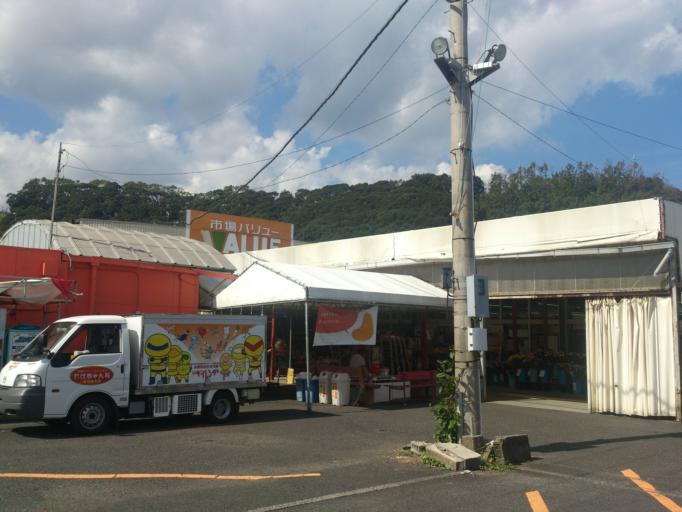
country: JP
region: Kagoshima
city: Ibusuki
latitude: 31.3733
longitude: 130.5426
